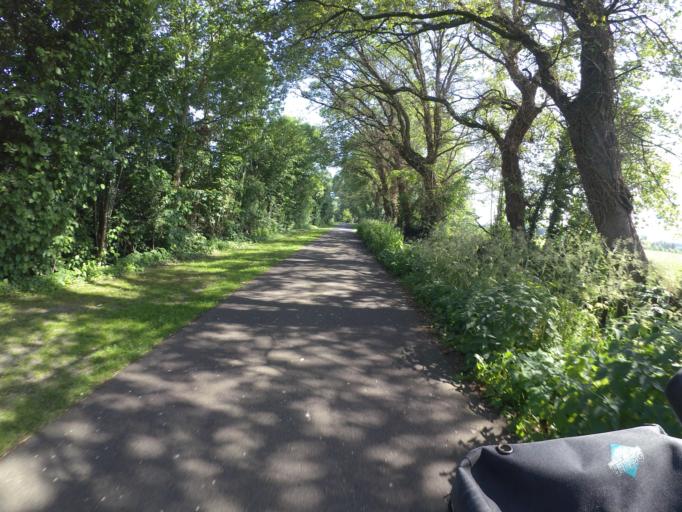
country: NL
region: Gelderland
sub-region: Berkelland
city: Eibergen
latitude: 52.0570
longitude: 6.6907
